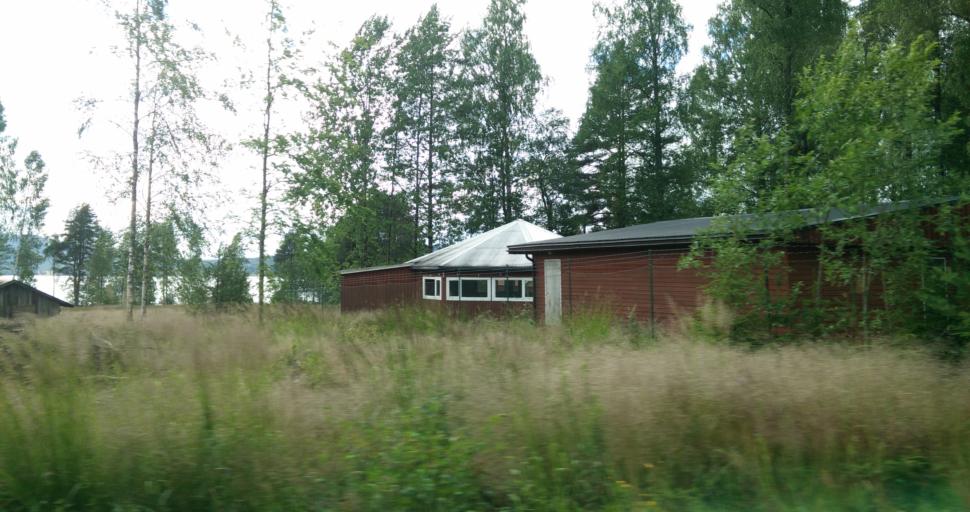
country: SE
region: Vaermland
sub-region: Munkfors Kommun
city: Munkfors
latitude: 59.9795
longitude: 13.4876
